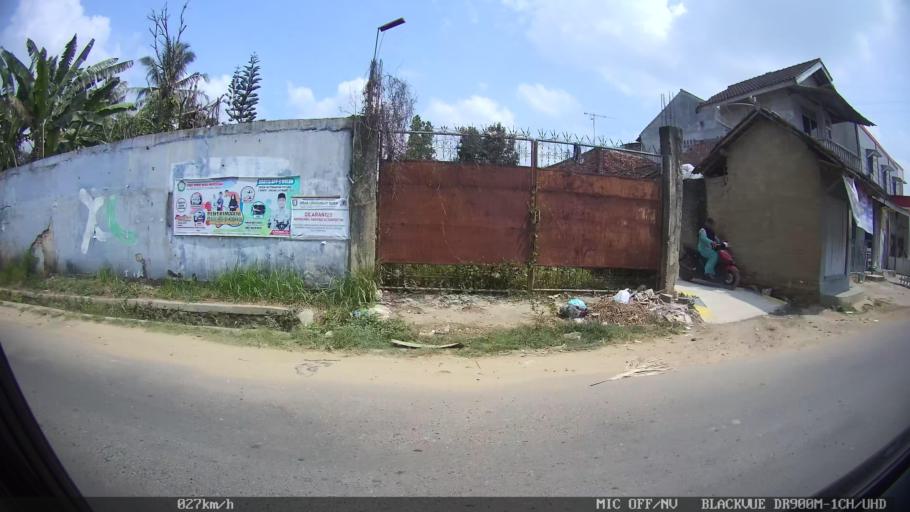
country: ID
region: Lampung
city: Pringsewu
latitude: -5.3660
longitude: 104.9713
